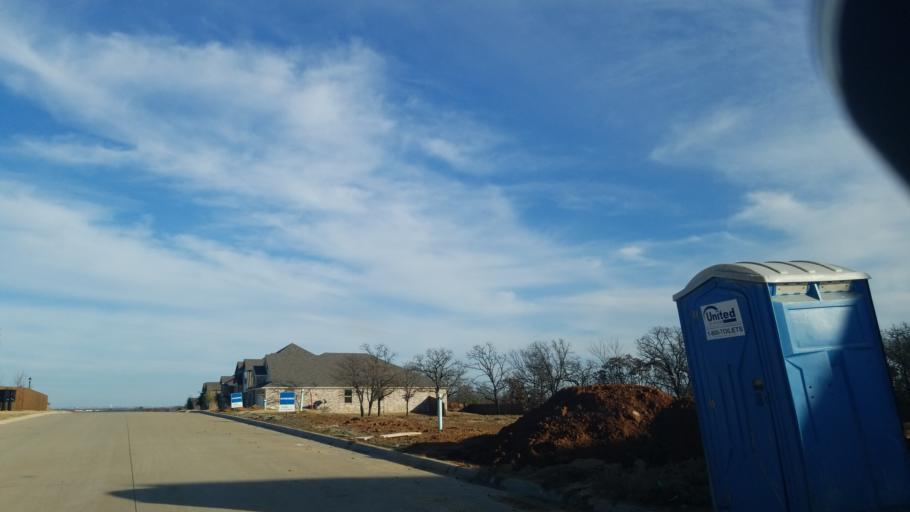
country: US
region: Texas
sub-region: Denton County
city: Corinth
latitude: 33.1454
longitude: -97.0786
